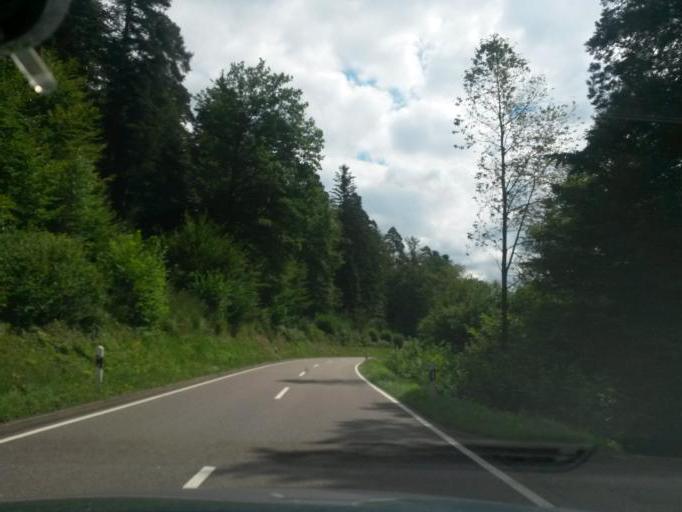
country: DE
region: Baden-Wuerttemberg
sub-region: Karlsruhe Region
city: Bad Herrenalb
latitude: 48.8507
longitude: 8.4594
